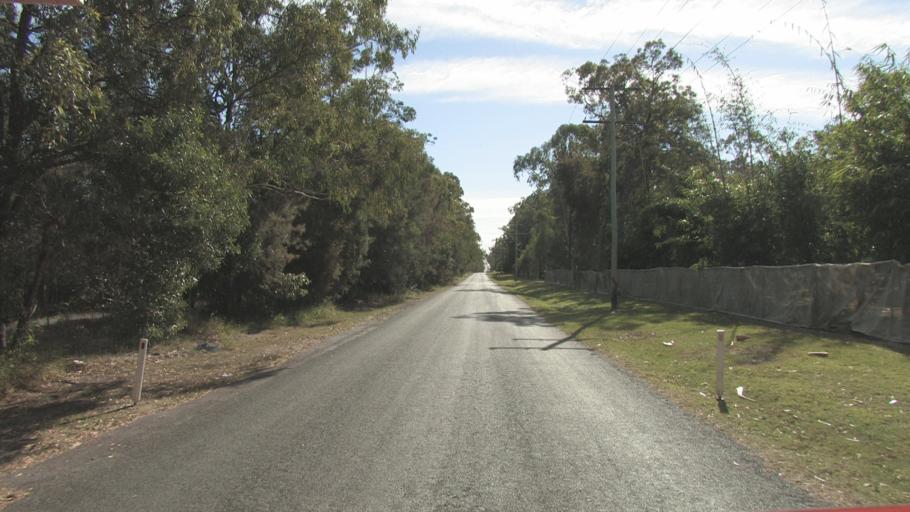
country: AU
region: Queensland
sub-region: Brisbane
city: Forest Lake
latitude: -27.6561
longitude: 152.9827
